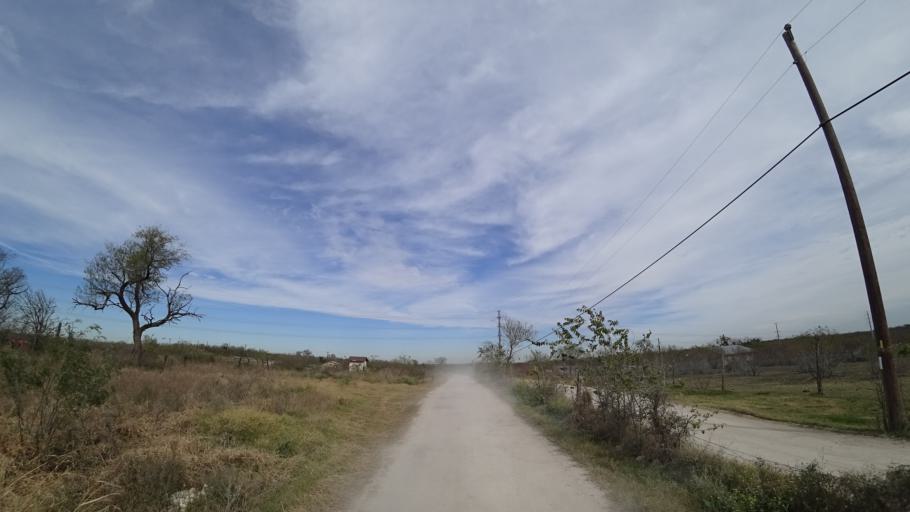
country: US
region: Texas
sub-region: Travis County
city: Garfield
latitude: 30.1535
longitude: -97.5953
